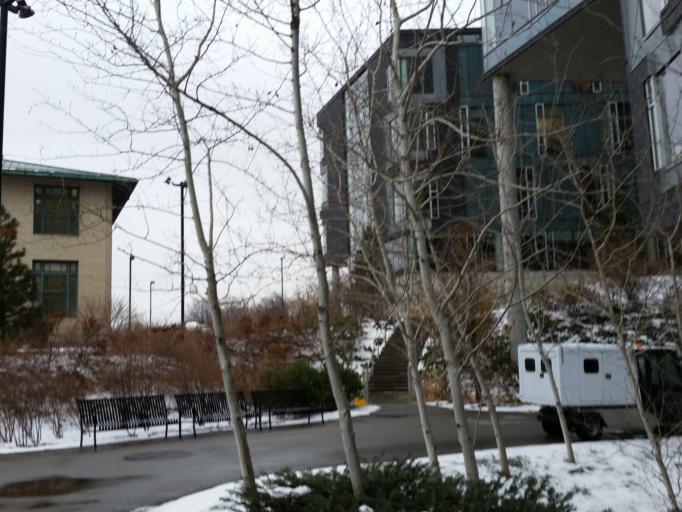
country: US
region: Pennsylvania
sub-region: Allegheny County
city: Bloomfield
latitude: 40.4433
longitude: -79.9449
